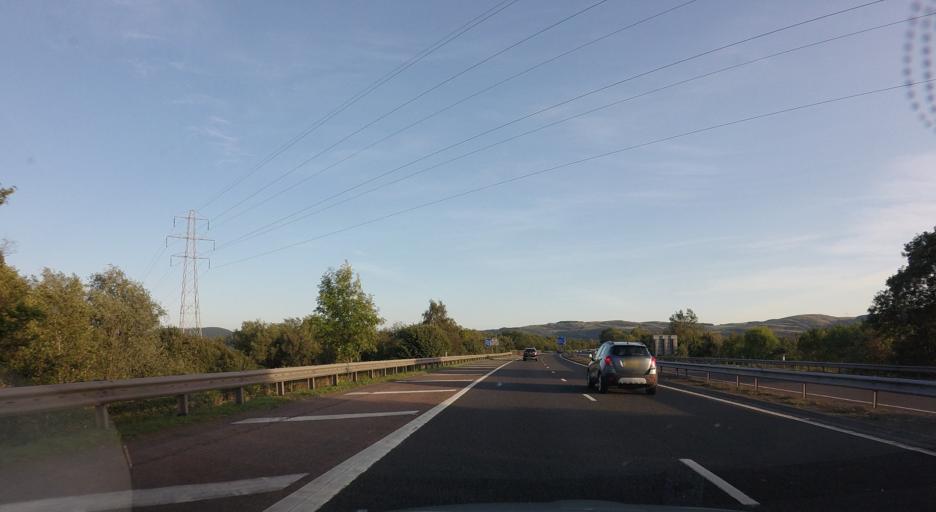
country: GB
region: Scotland
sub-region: Perth and Kinross
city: Bridge of Earn
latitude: 56.3510
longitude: -3.3977
